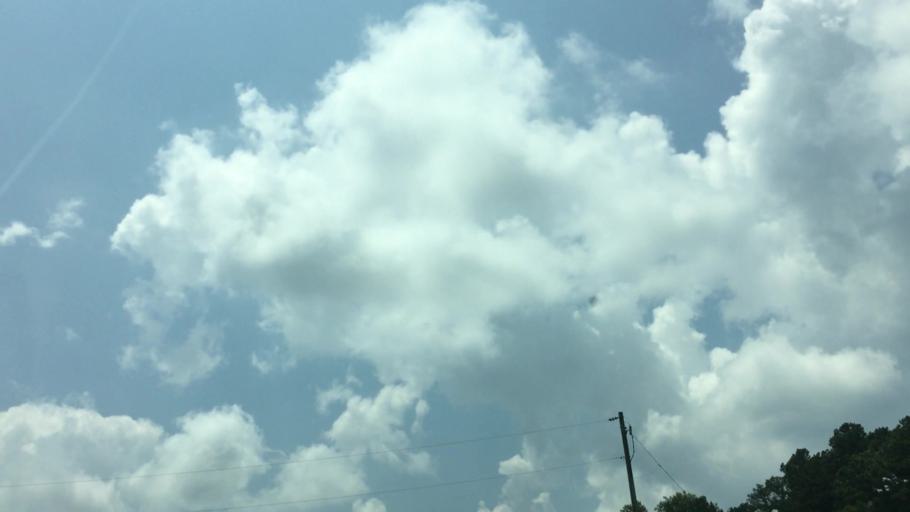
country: US
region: Georgia
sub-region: Carroll County
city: Villa Rica
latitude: 33.6118
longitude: -84.8937
